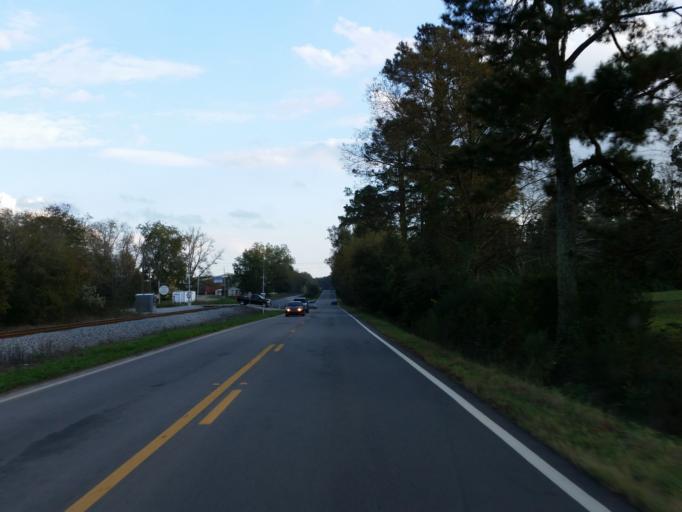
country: US
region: Georgia
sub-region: Monroe County
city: Forsyth
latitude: 32.9623
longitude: -83.8654
